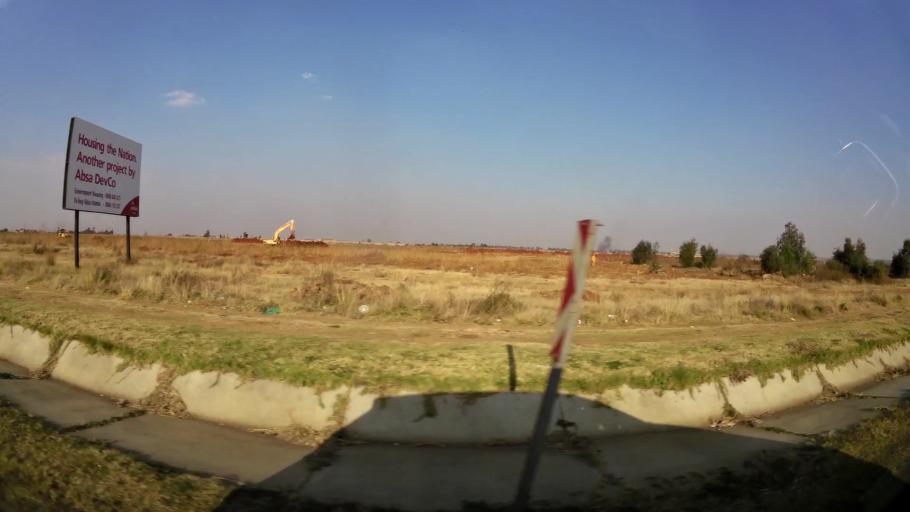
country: ZA
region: Gauteng
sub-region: Ekurhuleni Metropolitan Municipality
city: Benoni
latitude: -26.1455
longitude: 28.3860
